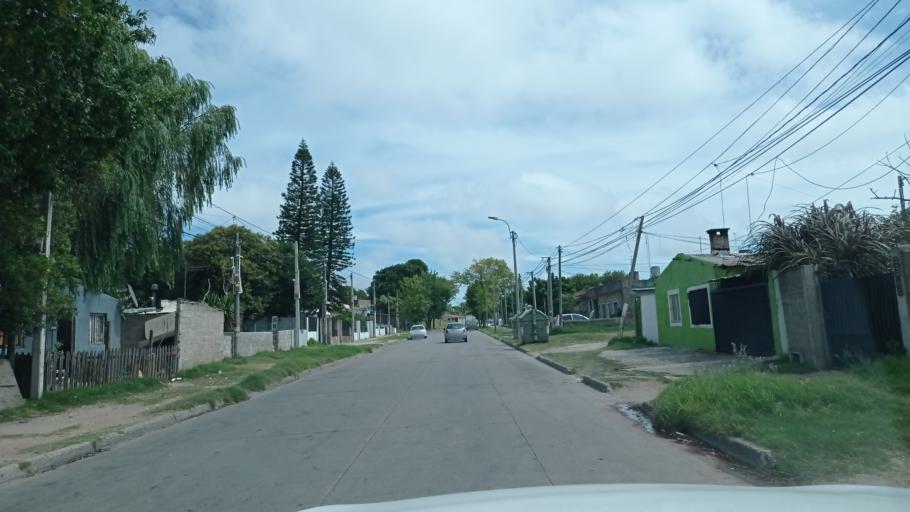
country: UY
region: Montevideo
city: Montevideo
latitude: -34.8663
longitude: -56.1252
